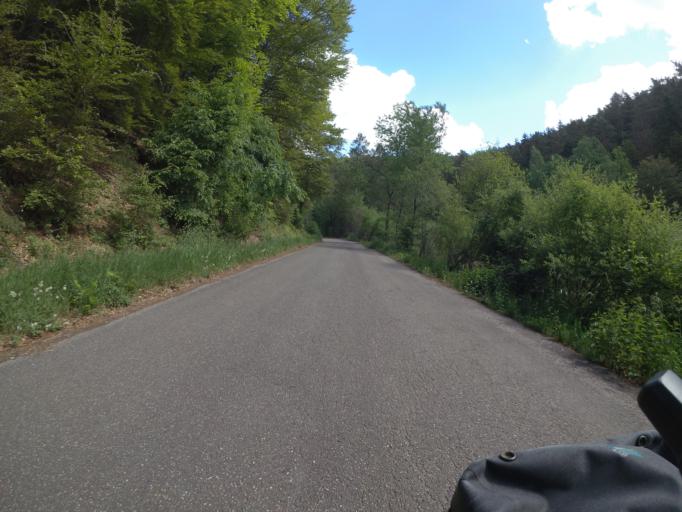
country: DE
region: Rheinland-Pfalz
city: Dahn
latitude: 49.1586
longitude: 7.7570
